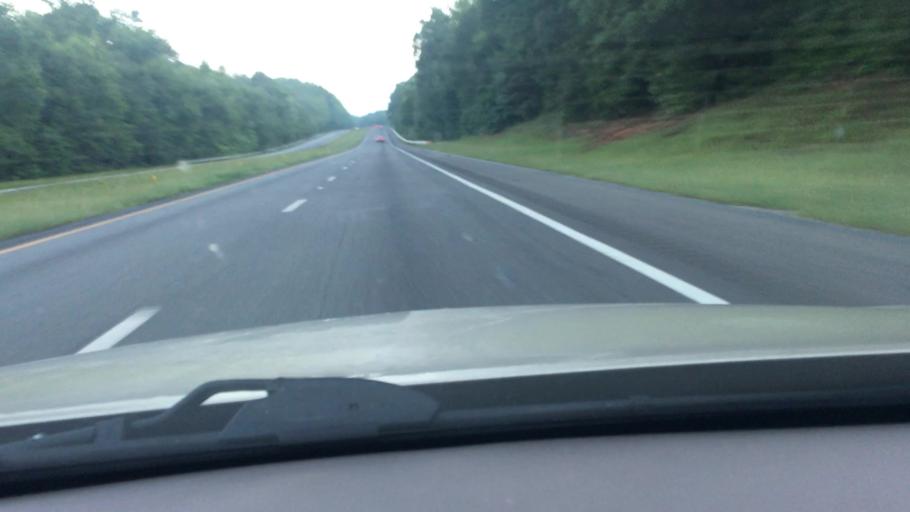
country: US
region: South Carolina
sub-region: Lexington County
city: Irmo
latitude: 34.1244
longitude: -81.2008
